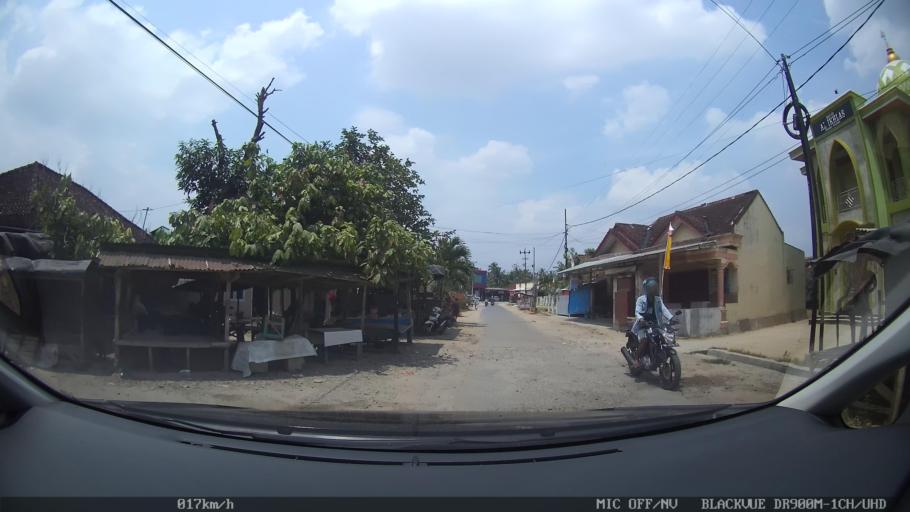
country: ID
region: Lampung
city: Pringsewu
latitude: -5.3475
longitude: 104.9859
